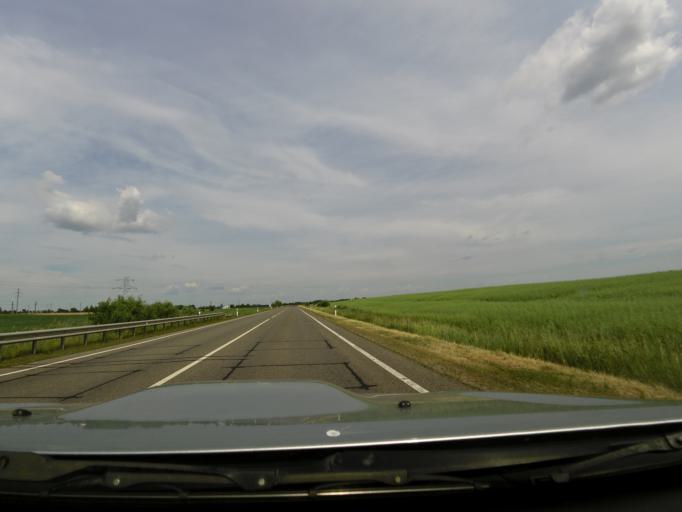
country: LT
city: Vilkaviskis
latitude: 54.6336
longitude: 23.0589
